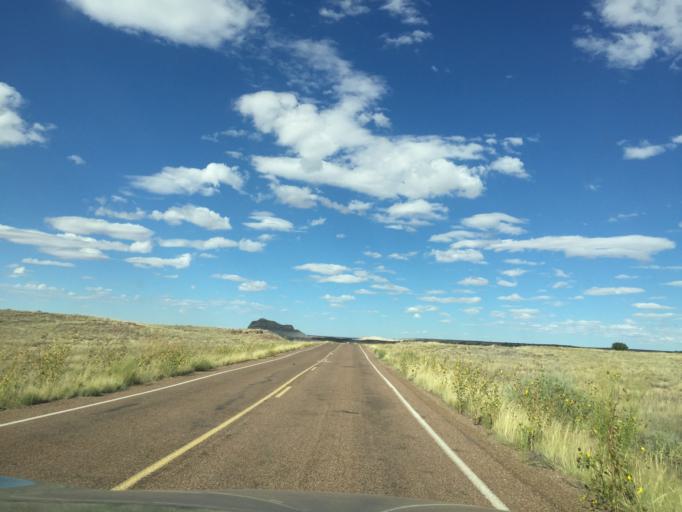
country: US
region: Arizona
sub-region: Navajo County
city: Holbrook
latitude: 34.8567
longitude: -109.7962
